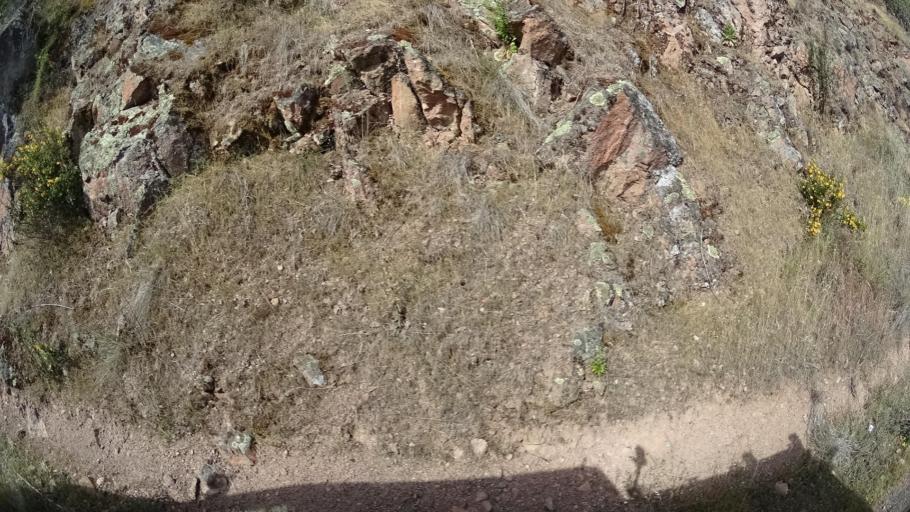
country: US
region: California
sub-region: Lake County
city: Soda Bay
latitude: 39.0073
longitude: -122.8010
